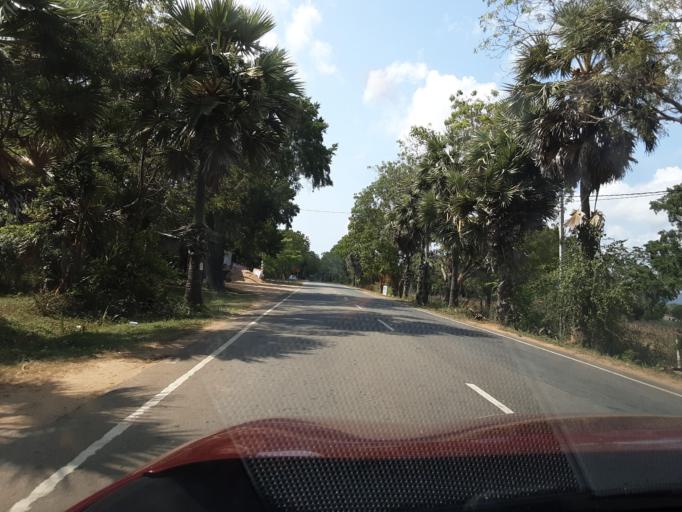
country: LK
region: Southern
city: Tangalla
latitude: 6.2619
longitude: 81.2261
